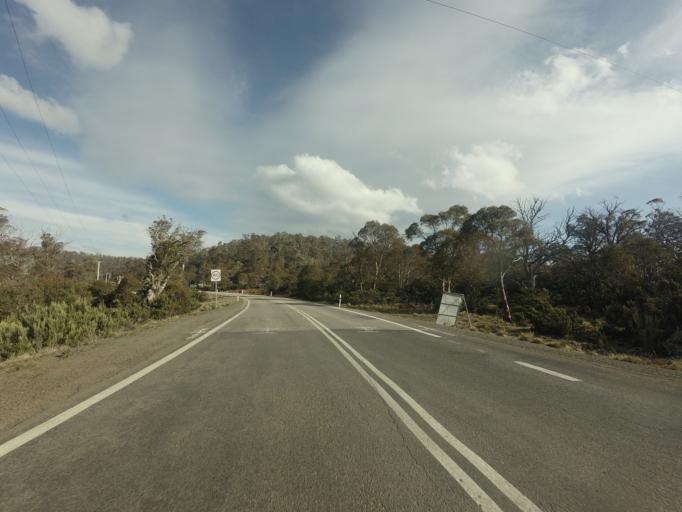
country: AU
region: Tasmania
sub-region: Meander Valley
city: Deloraine
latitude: -41.9812
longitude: 146.6792
